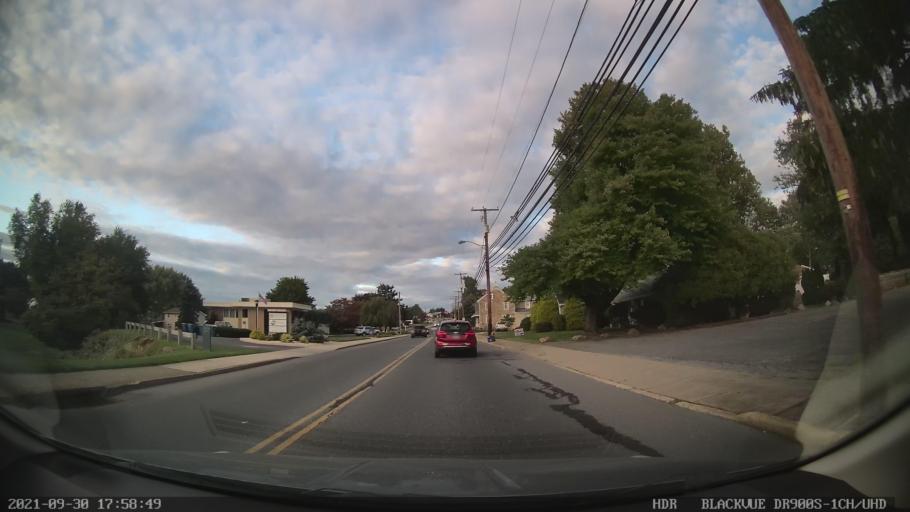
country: US
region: Pennsylvania
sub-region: Lehigh County
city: Emmaus
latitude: 40.5451
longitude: -75.4919
